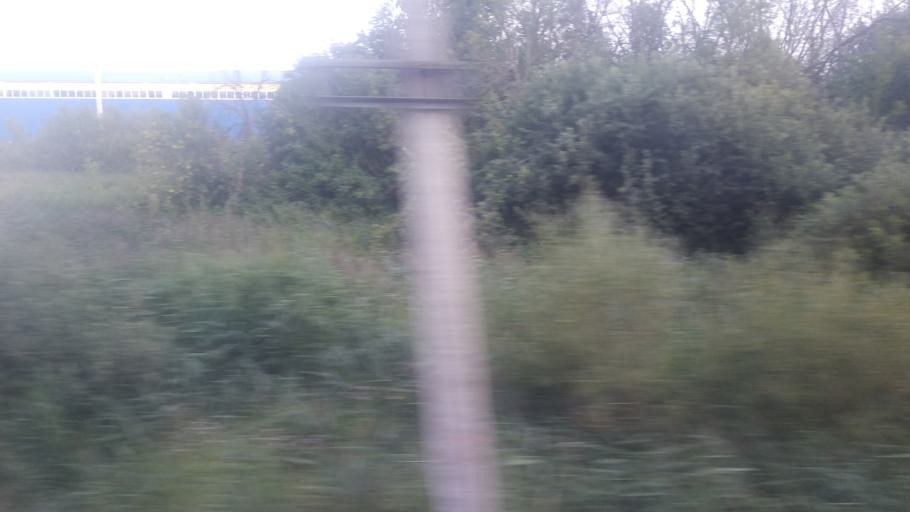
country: RU
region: Moskovskaya
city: Tugolesskiy Bor
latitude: 55.5543
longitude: 39.6990
